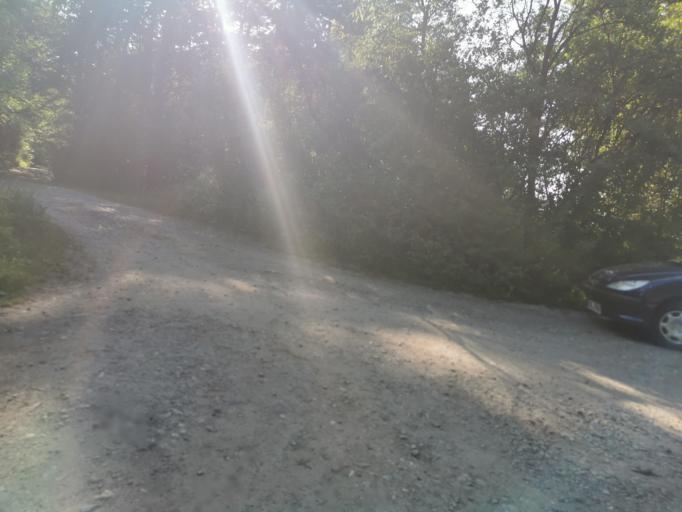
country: CZ
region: South Moravian
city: Knezdub
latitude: 48.8699
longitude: 17.4084
